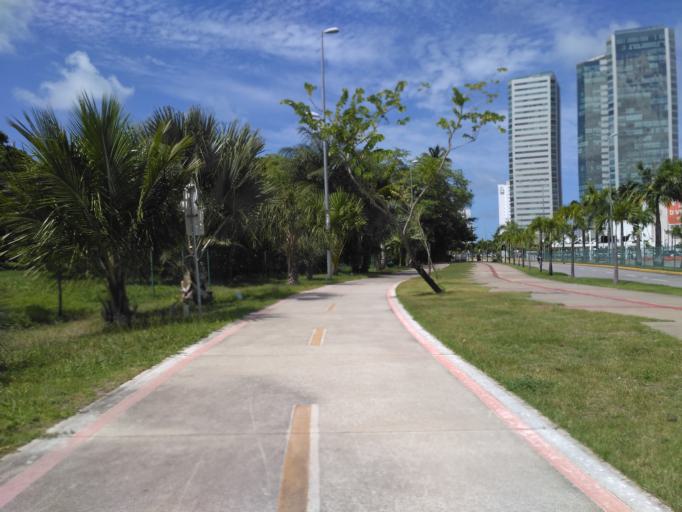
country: BR
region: Pernambuco
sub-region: Recife
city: Recife
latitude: -8.0846
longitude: -34.8942
